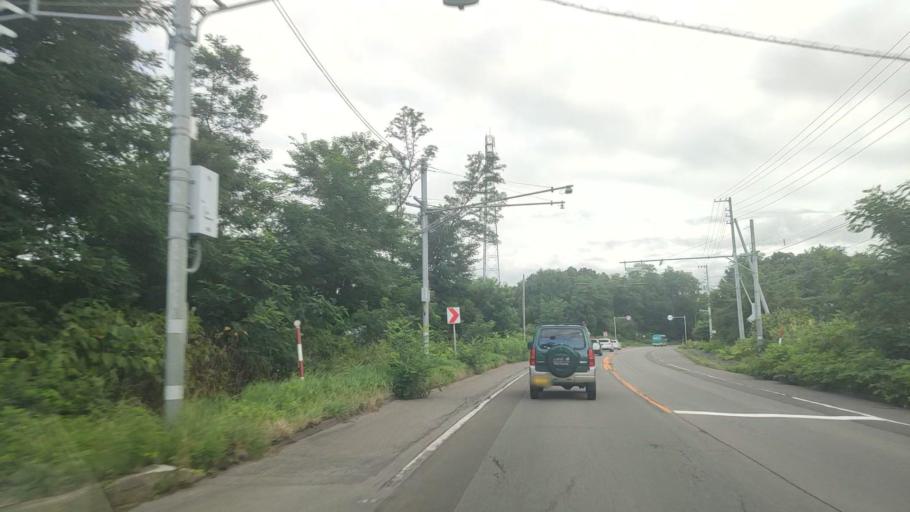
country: JP
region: Hokkaido
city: Nanae
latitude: 42.0672
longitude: 140.6032
